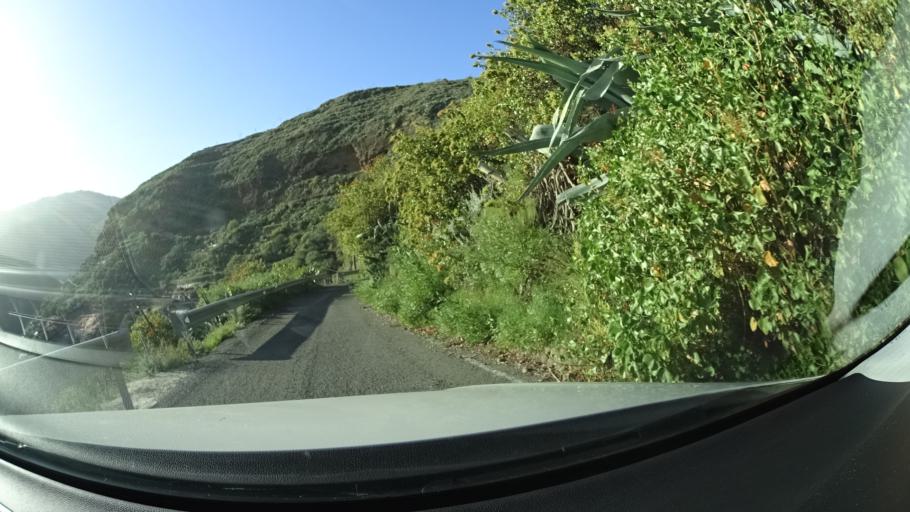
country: ES
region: Canary Islands
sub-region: Provincia de Las Palmas
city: Artenara
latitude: 28.0455
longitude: -15.6594
